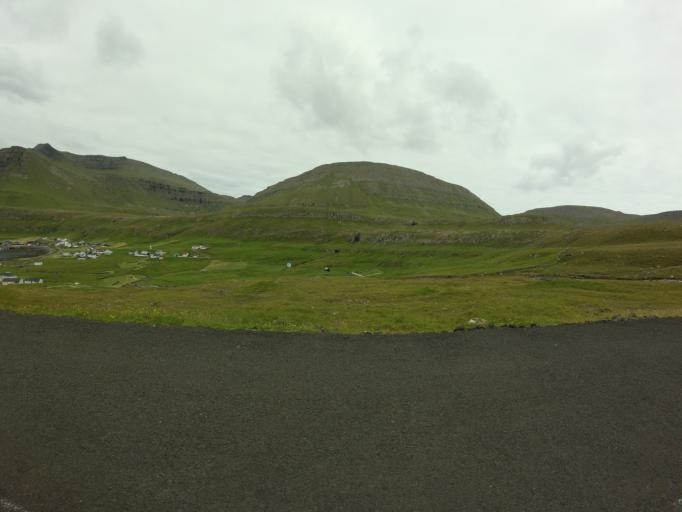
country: FO
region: Suduroy
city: Tvoroyri
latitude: 61.5178
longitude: -6.8766
